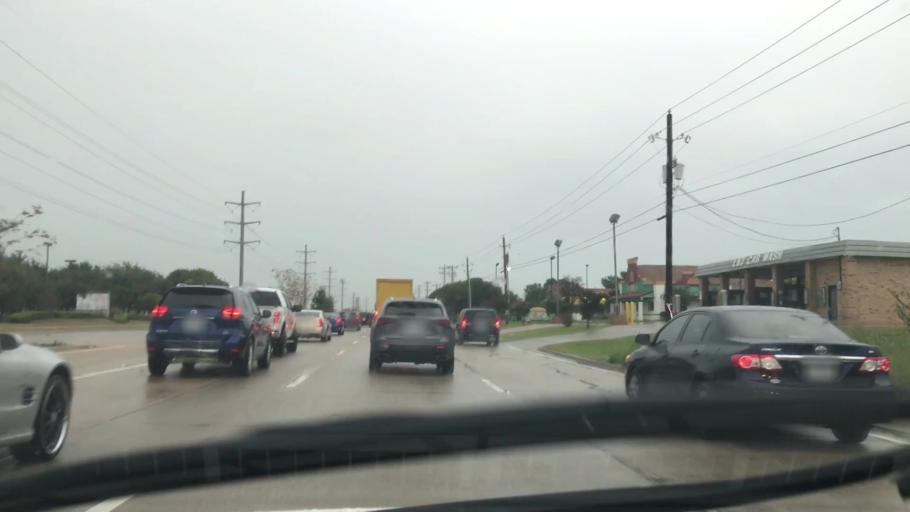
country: US
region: Texas
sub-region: Dallas County
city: Rowlett
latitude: 32.9151
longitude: -96.5221
